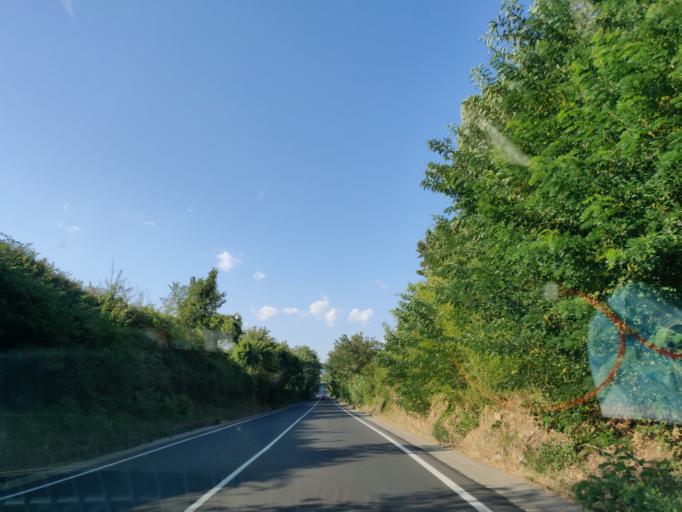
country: IT
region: Latium
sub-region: Provincia di Viterbo
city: Valentano
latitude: 42.5751
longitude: 11.8315
